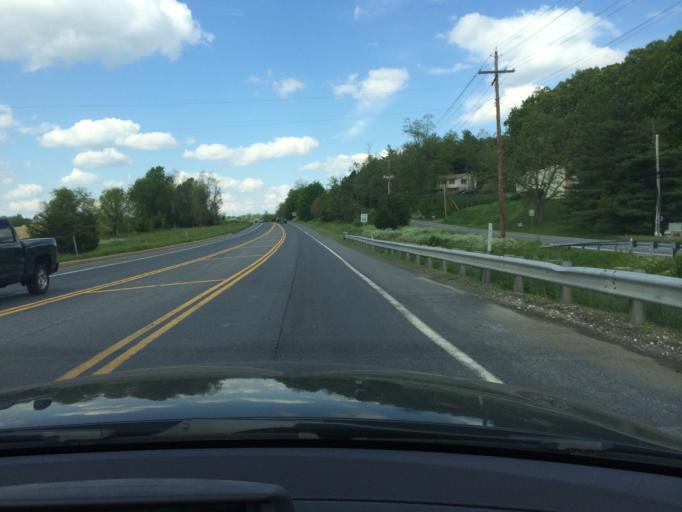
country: US
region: Maryland
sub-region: Carroll County
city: Westminster
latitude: 39.5679
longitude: -77.0205
